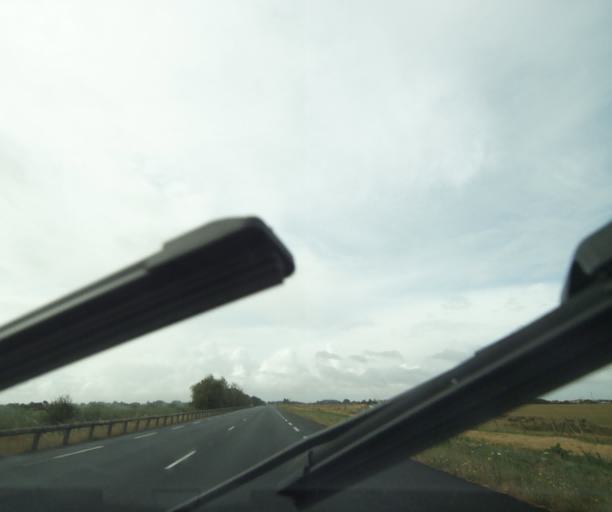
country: FR
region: Pays de la Loire
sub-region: Departement de la Vendee
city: Champagne-les-Marais
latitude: 46.3877
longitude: -1.0933
